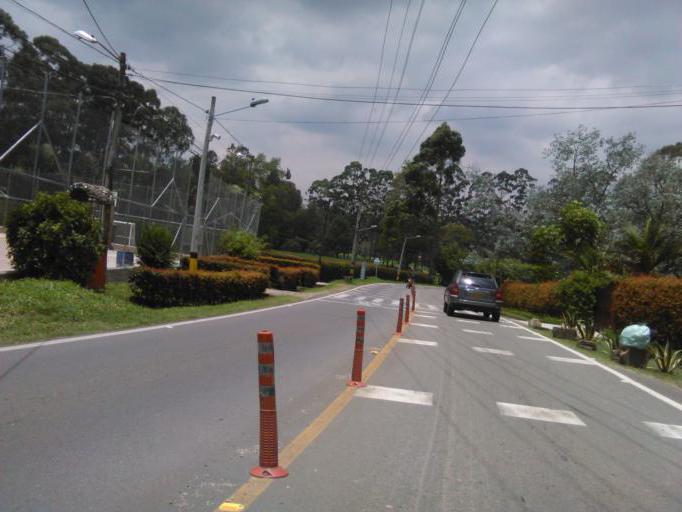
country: CO
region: Antioquia
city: La Ceja
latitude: 6.0221
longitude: -75.4101
